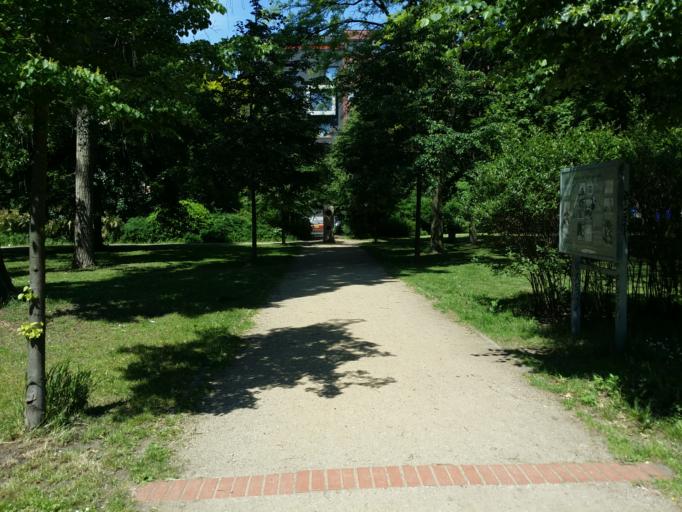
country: DE
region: Berlin
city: Bezirk Kreuzberg
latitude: 52.5088
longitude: 13.4076
